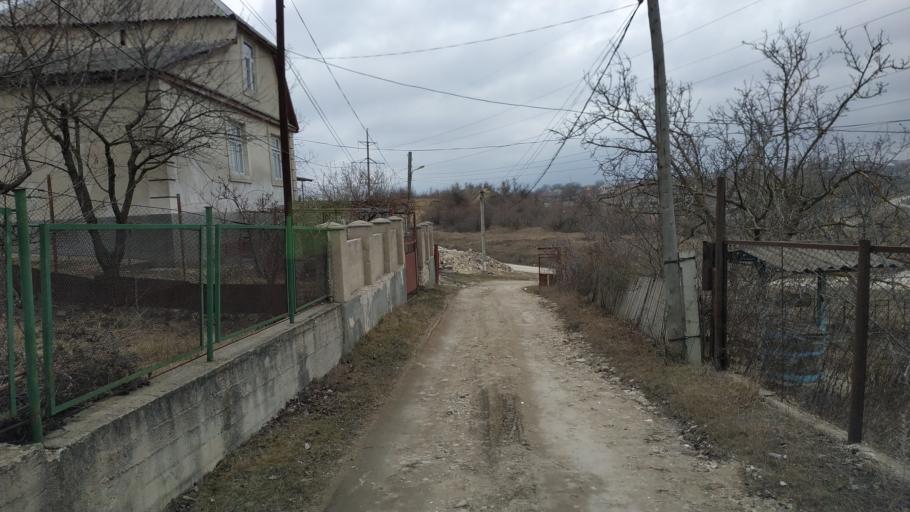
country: MD
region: Laloveni
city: Ialoveni
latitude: 46.9314
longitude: 28.7948
